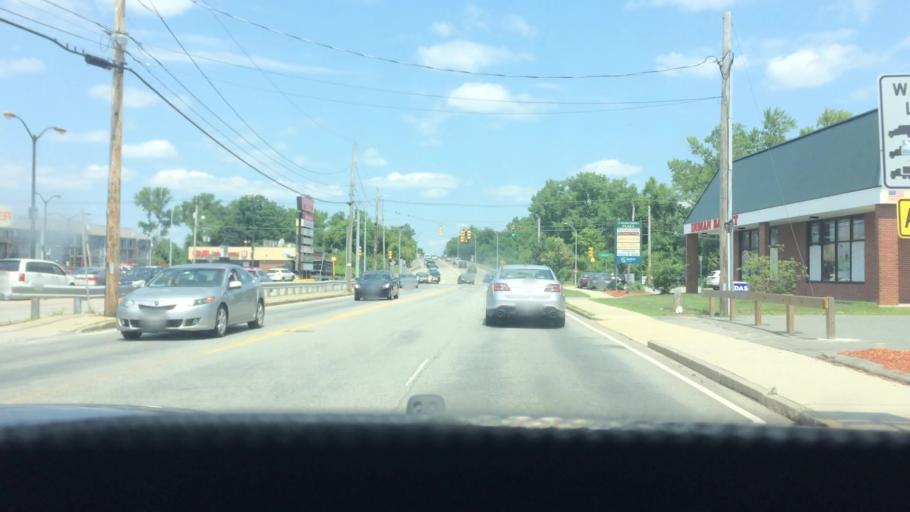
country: US
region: Massachusetts
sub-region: Middlesex County
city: Chelmsford
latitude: 42.6339
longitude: -71.3555
